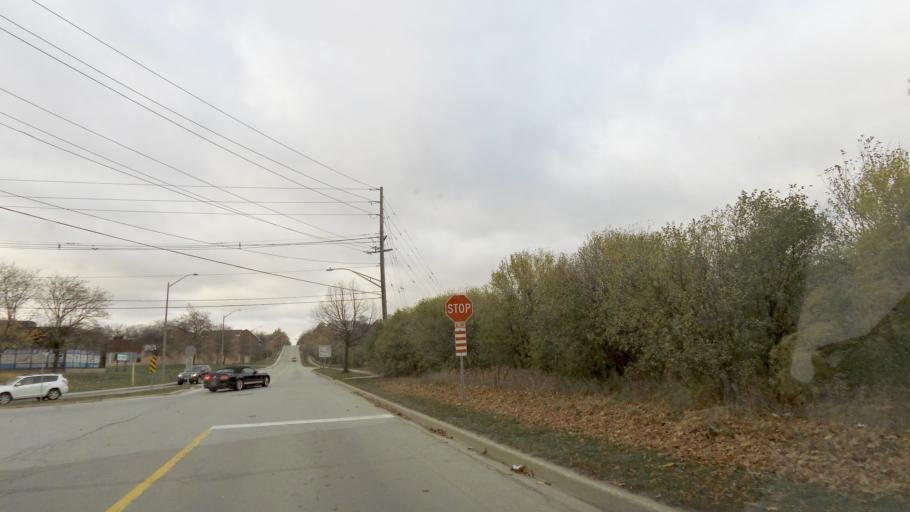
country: CA
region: Ontario
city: Oakville
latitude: 43.4694
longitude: -79.6798
